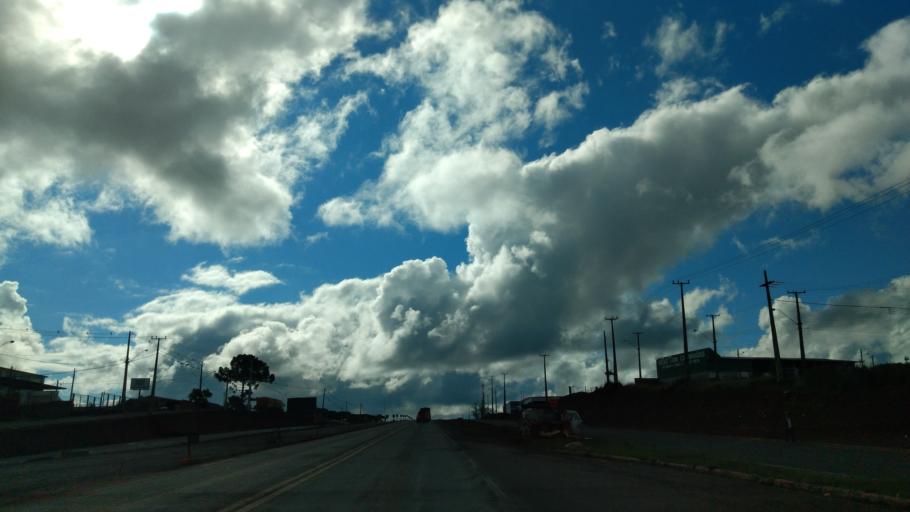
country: BR
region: Parana
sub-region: Guarapuava
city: Guarapuava
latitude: -25.3470
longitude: -51.4890
